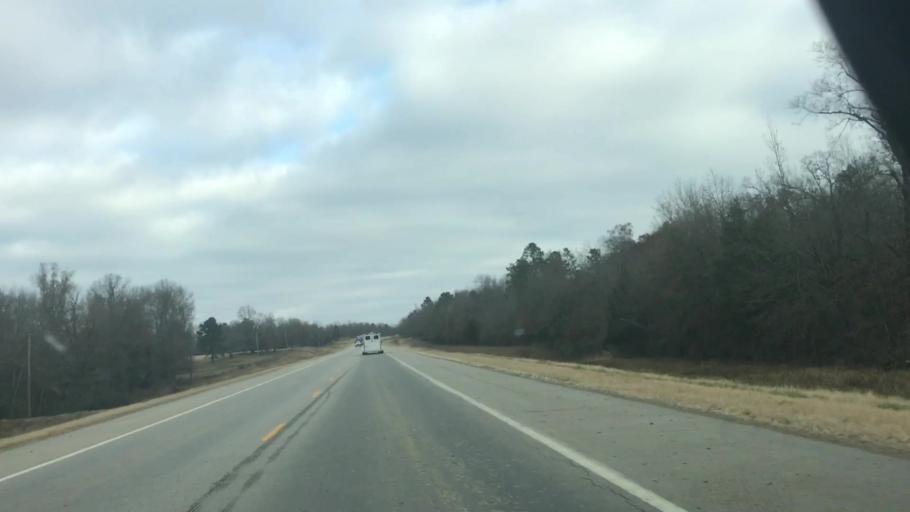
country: US
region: Arkansas
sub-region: Scott County
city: Waldron
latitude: 34.9150
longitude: -94.1071
